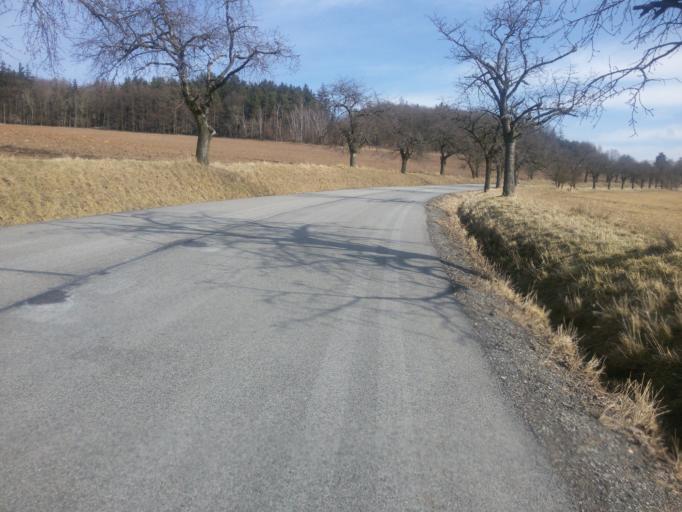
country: CZ
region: South Moravian
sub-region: Okres Brno-Venkov
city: Lomnice
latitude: 49.4208
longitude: 16.4014
